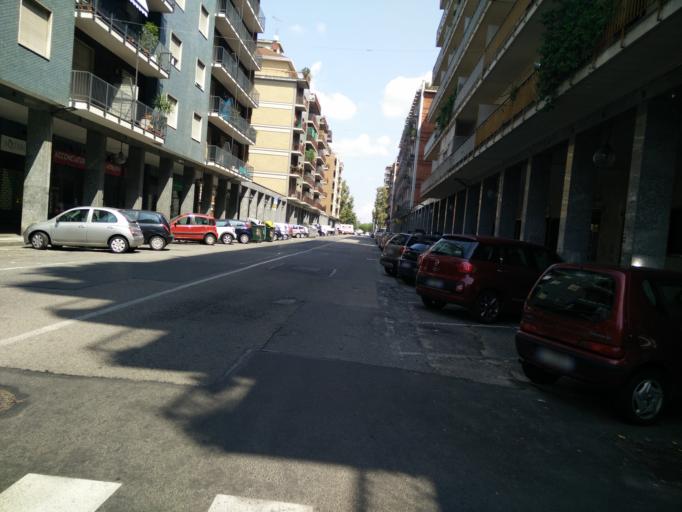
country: IT
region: Piedmont
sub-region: Provincia di Torino
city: Nichelino
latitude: 45.0223
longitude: 7.6423
